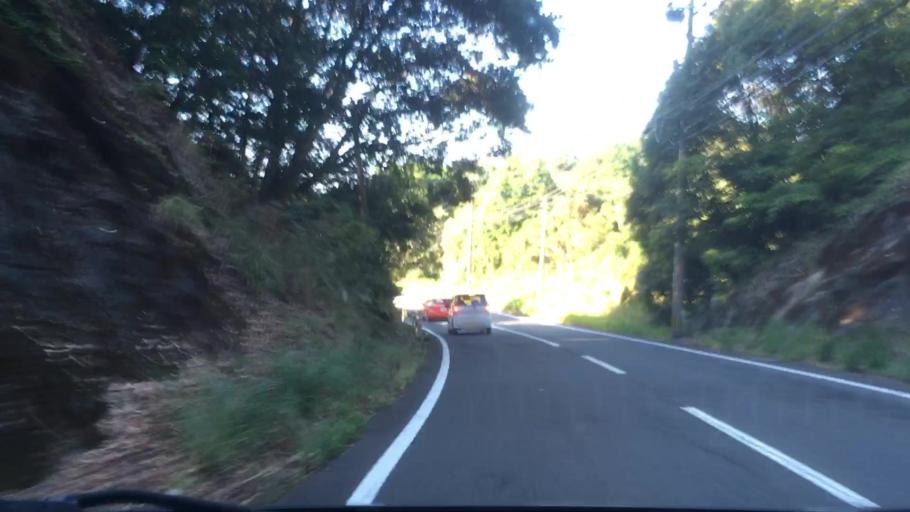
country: JP
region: Nagasaki
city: Sasebo
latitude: 32.9624
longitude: 129.6860
